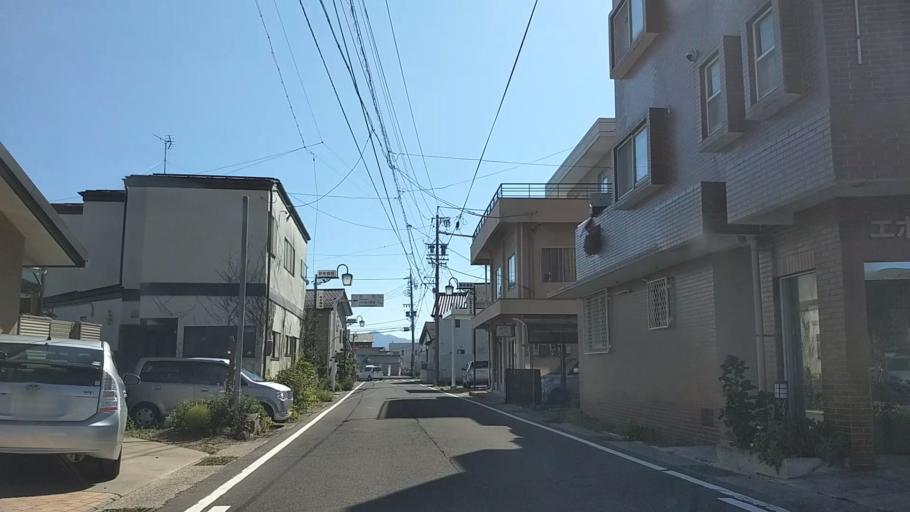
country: JP
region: Nagano
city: Nagano-shi
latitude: 36.6152
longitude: 138.1519
